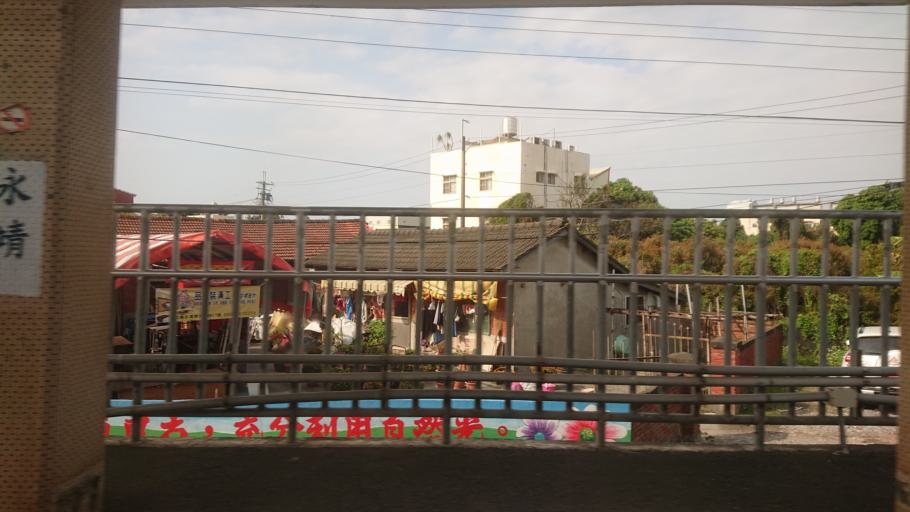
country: TW
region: Taiwan
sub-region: Nantou
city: Nantou
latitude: 23.9286
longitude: 120.5716
